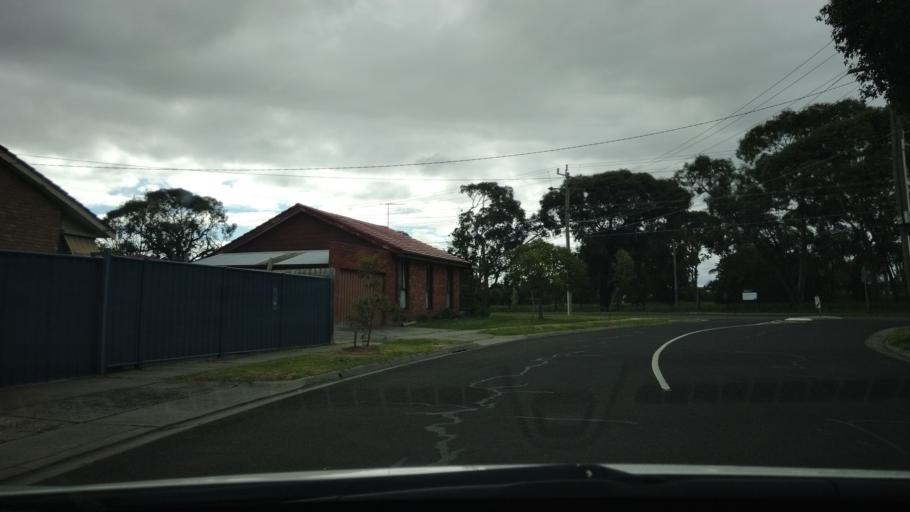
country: AU
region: Victoria
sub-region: Greater Dandenong
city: Springvale South
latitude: -37.9832
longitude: 145.1518
